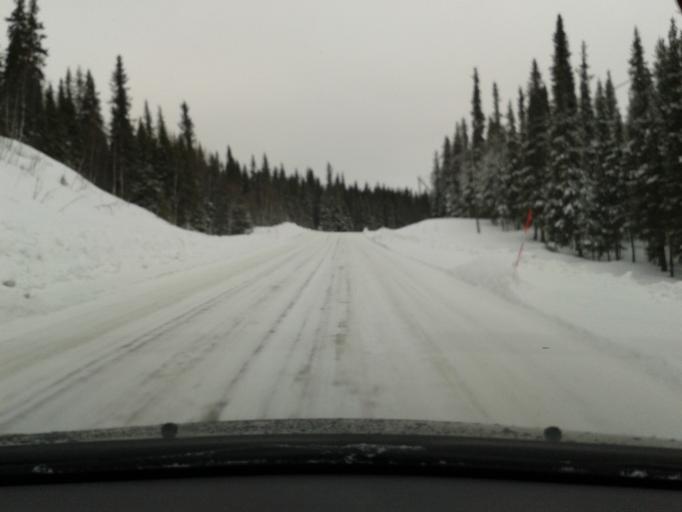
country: SE
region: Vaesterbotten
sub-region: Vilhelmina Kommun
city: Sjoberg
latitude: 65.2315
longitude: 15.9772
